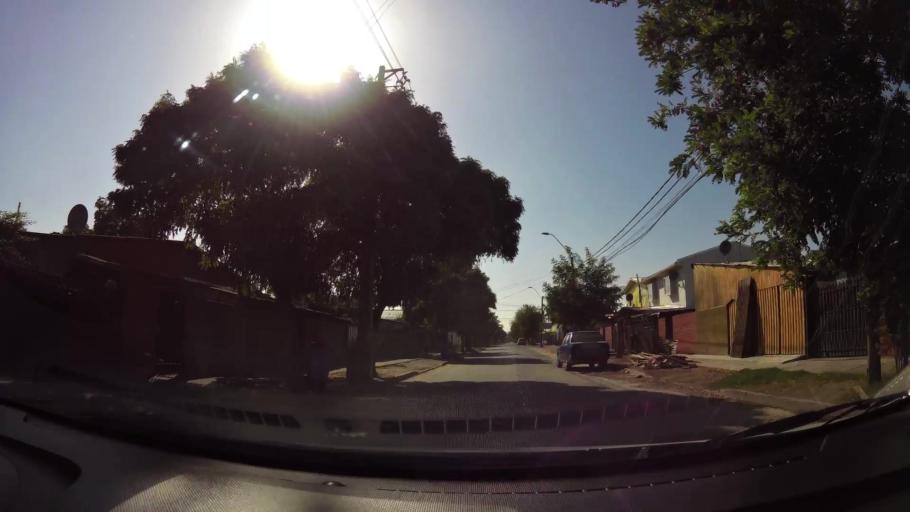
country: CL
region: Maule
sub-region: Provincia de Talca
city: Talca
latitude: -35.4012
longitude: -71.6563
